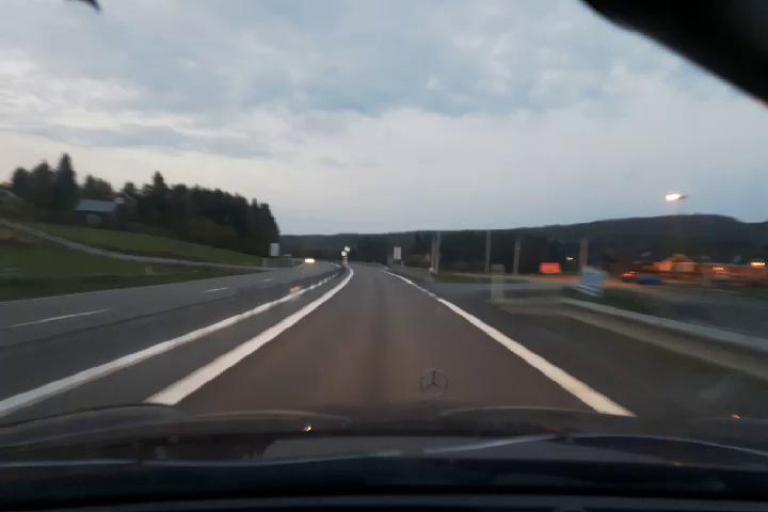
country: SE
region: Vaesternorrland
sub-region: Kramfors Kommun
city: Nordingra
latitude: 62.9704
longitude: 18.1601
